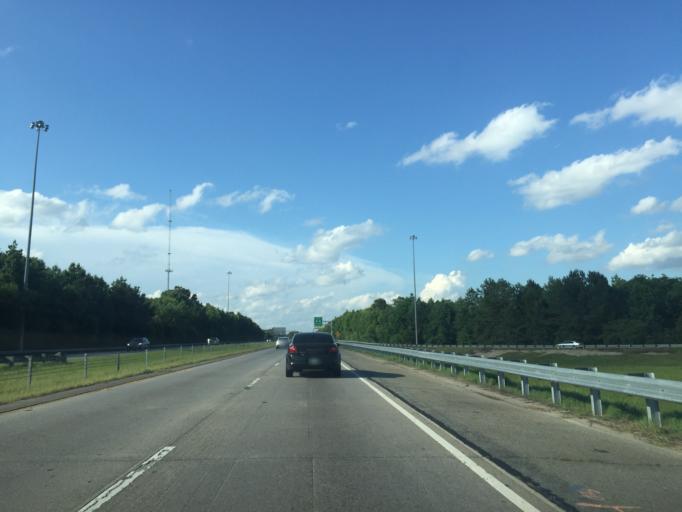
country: US
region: Georgia
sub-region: Chatham County
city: Savannah
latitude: 32.0451
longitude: -81.1459
